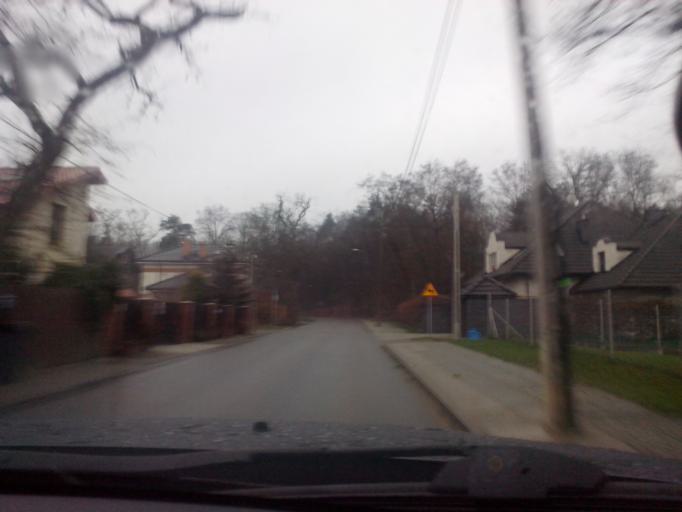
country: PL
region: Masovian Voivodeship
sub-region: Warszawa
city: Bialoleka
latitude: 52.3400
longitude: 20.9784
